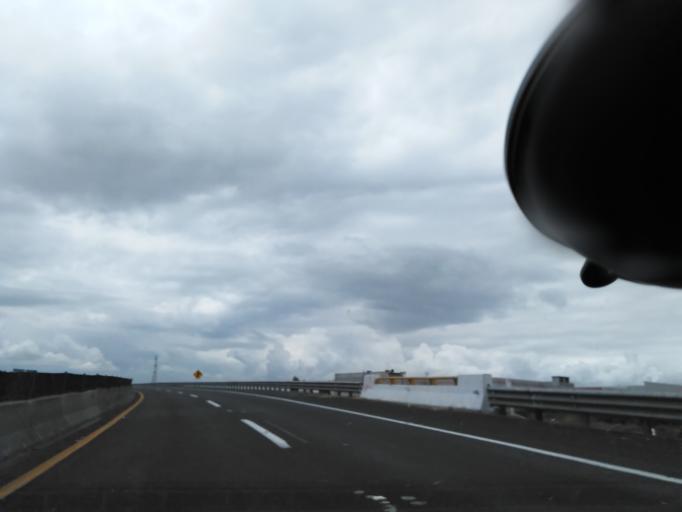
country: MX
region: Mexico
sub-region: Huehuetoca
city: Jorobas
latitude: 19.8241
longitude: -99.2312
